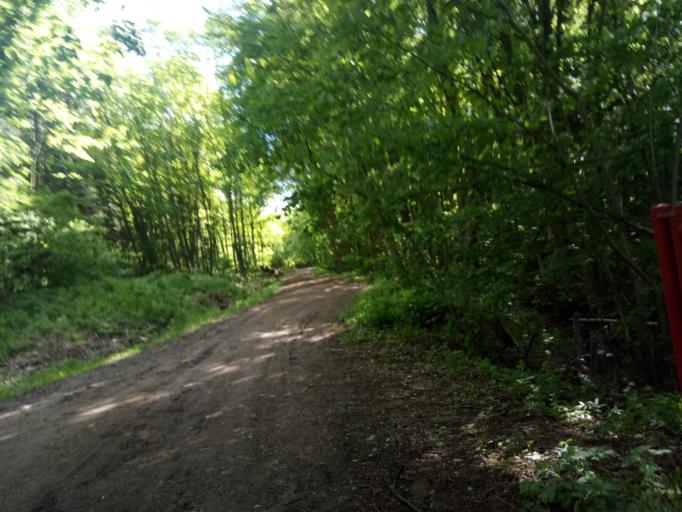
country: AT
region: Lower Austria
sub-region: Politischer Bezirk Modling
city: Breitenfurt bei Wien
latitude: 48.1277
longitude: 16.1455
